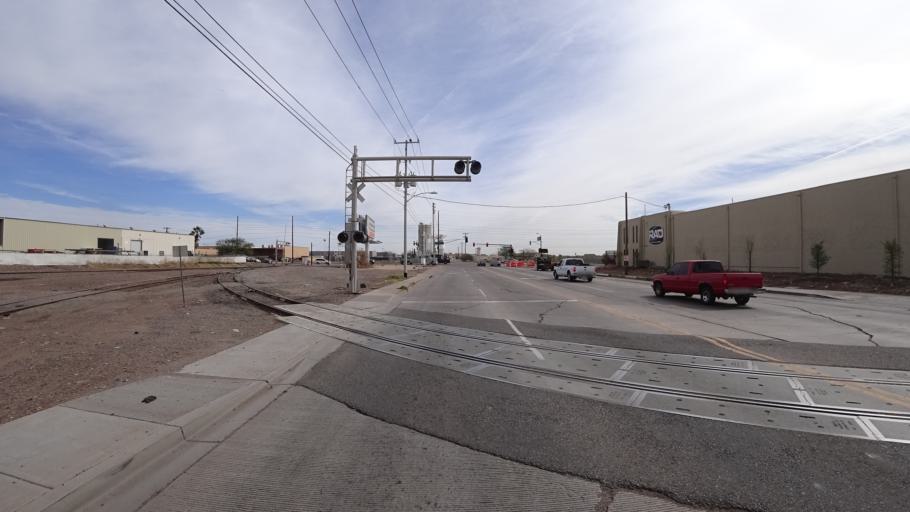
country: US
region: Arizona
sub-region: Maricopa County
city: Phoenix
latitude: 33.4223
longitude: -112.1009
